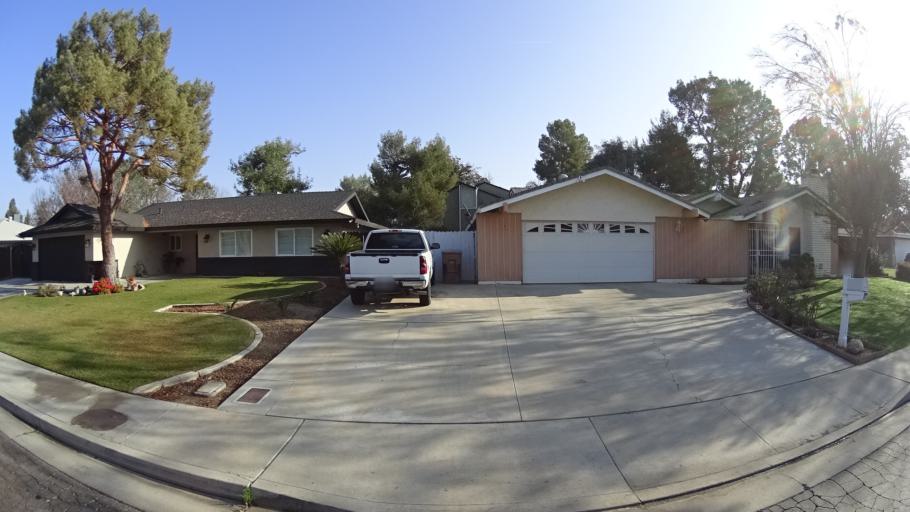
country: US
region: California
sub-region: Kern County
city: Bakersfield
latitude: 35.3374
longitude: -119.0659
